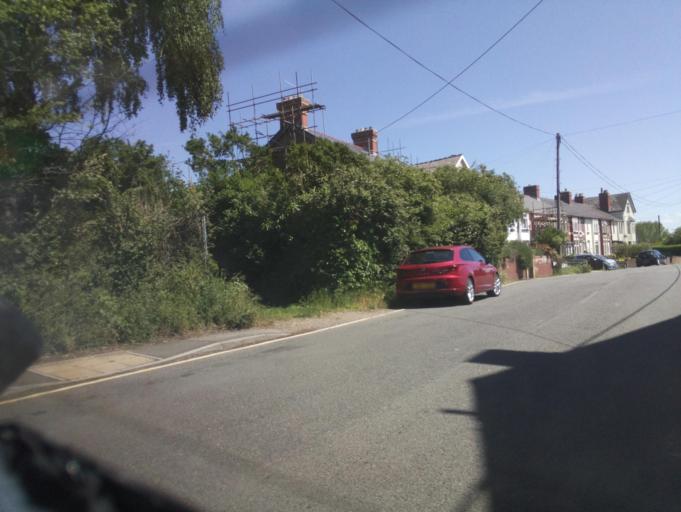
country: GB
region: Wales
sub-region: Monmouthshire
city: Rogiet
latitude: 51.5854
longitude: -2.7820
